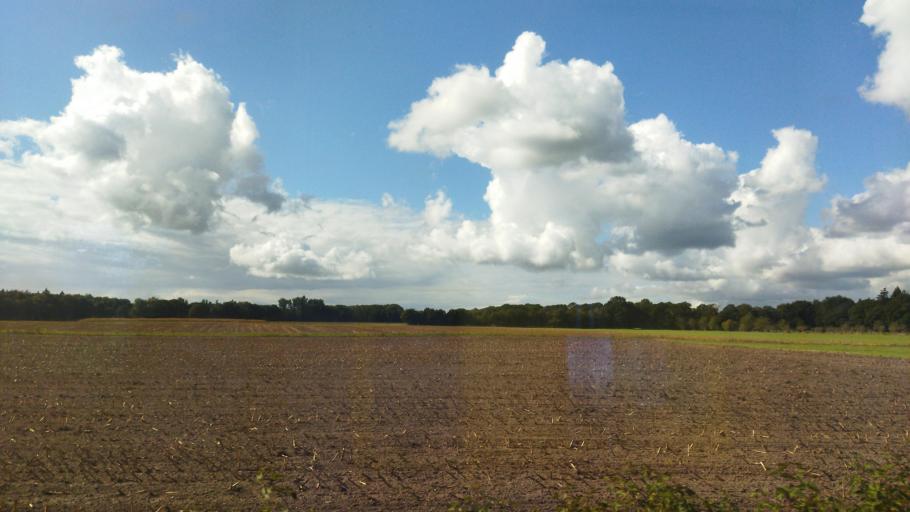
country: DE
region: Lower Saxony
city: Lehe
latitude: 53.0177
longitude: 7.3435
